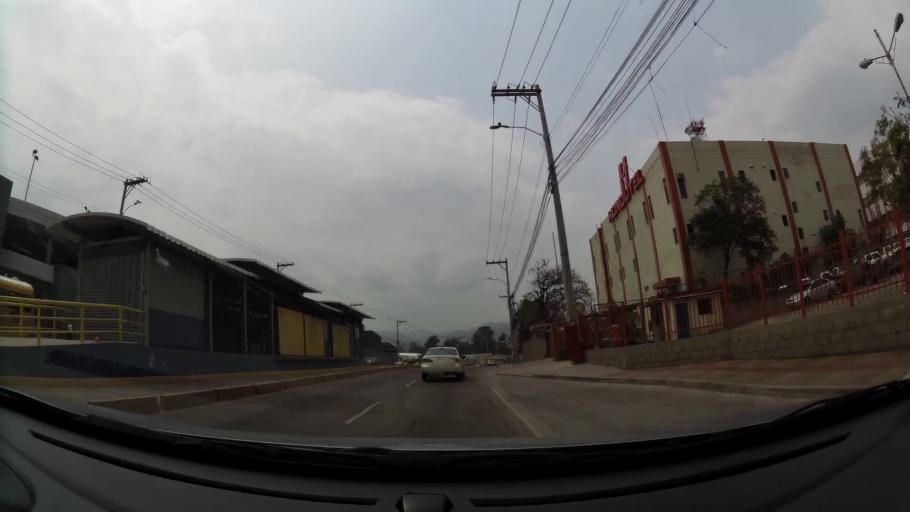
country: HN
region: Francisco Morazan
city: Tegucigalpa
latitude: 14.0841
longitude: -87.1866
